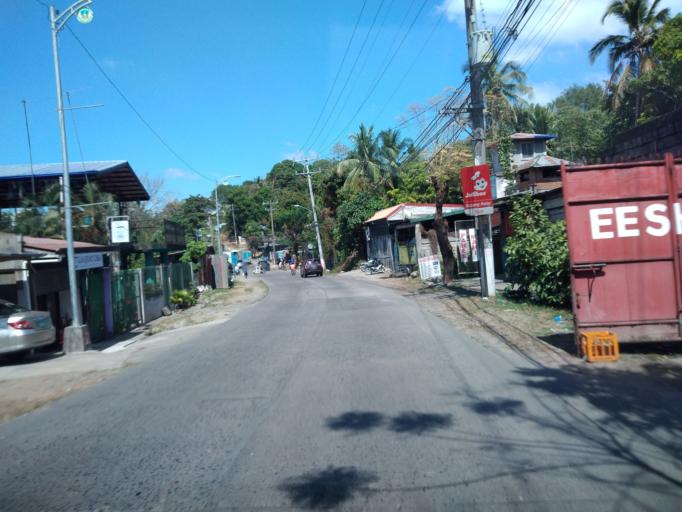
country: PH
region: Central Luzon
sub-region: Province of Bulacan
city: Bitungol
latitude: 14.8576
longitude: 121.0715
